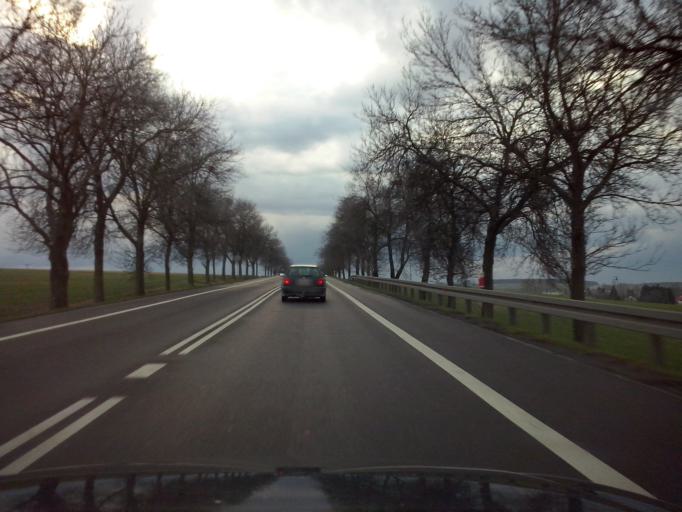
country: PL
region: Lublin Voivodeship
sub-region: Powiat chelmski
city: Rejowiec
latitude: 51.1670
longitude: 23.3619
